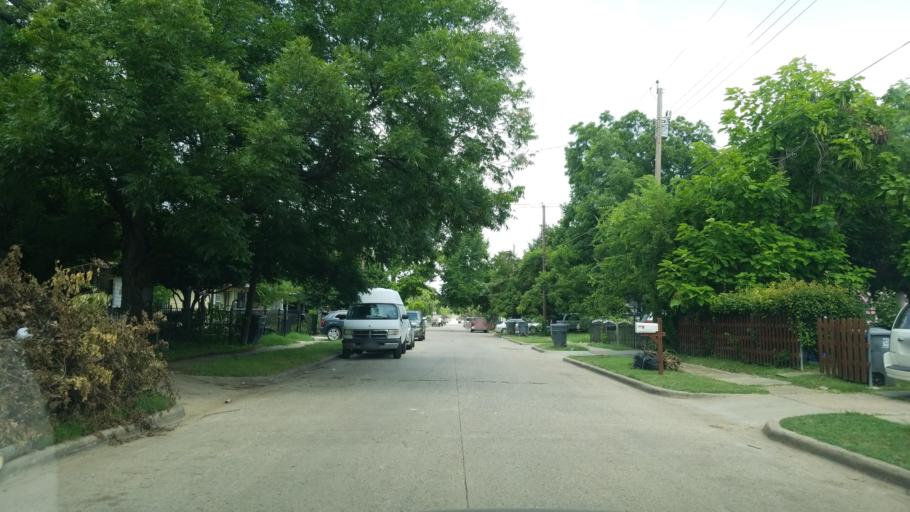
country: US
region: Texas
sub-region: Dallas County
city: Cockrell Hill
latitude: 32.7839
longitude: -96.8819
